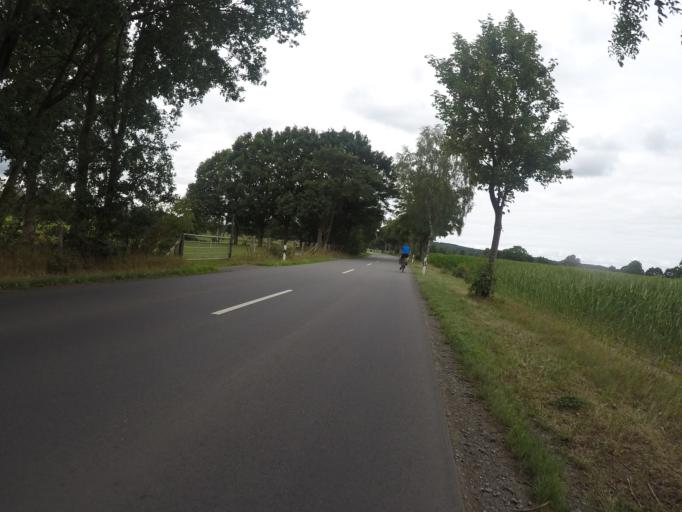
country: DE
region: Lower Saxony
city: Wingst
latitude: 53.7007
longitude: 9.0794
